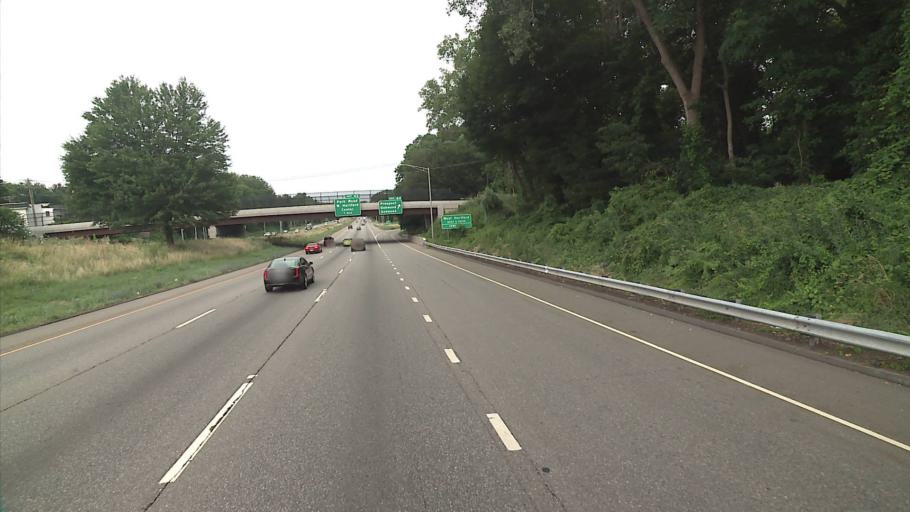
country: US
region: Connecticut
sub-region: Hartford County
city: West Hartford
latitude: 41.7501
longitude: -72.7141
